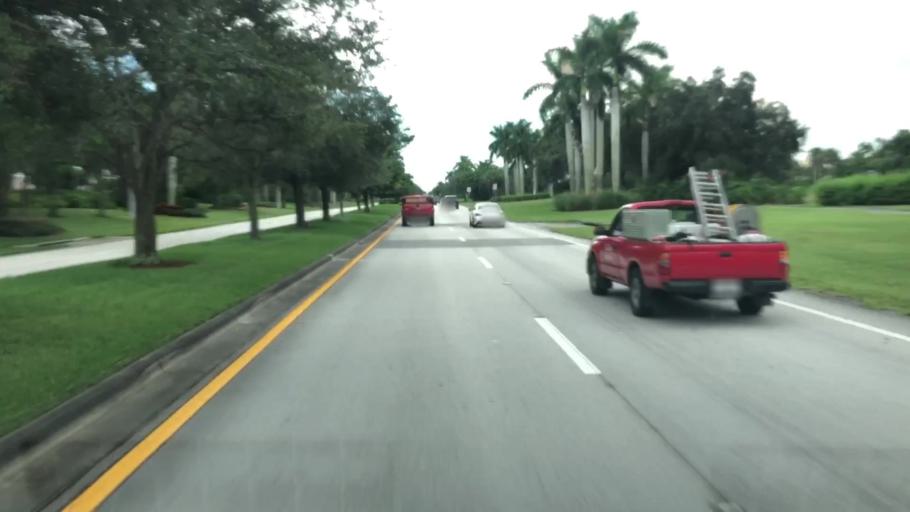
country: US
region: Florida
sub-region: Broward County
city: Parkland
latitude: 26.3185
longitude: -80.2790
